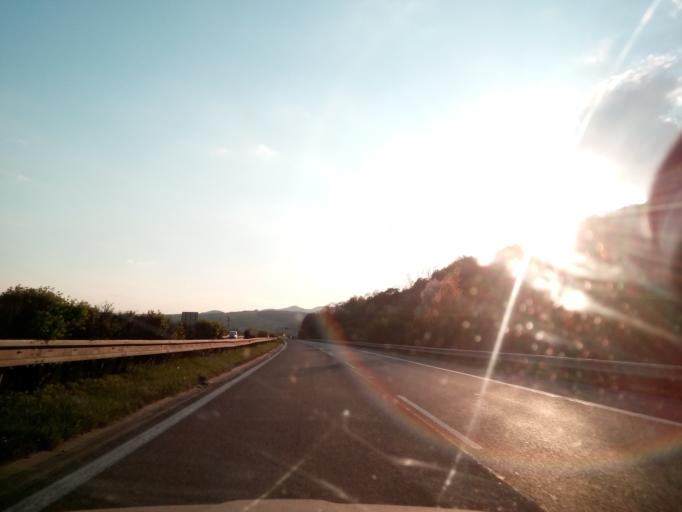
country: SK
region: Trenciansky
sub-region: Okres Trencin
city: Trencin
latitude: 48.9137
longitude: 18.0281
